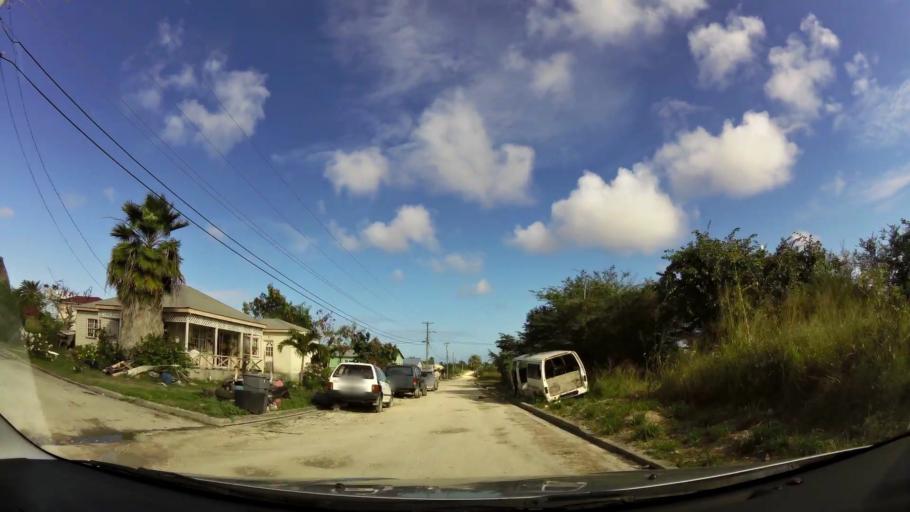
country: AG
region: Saint Peter
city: All Saints
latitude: 17.0669
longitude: -61.7866
